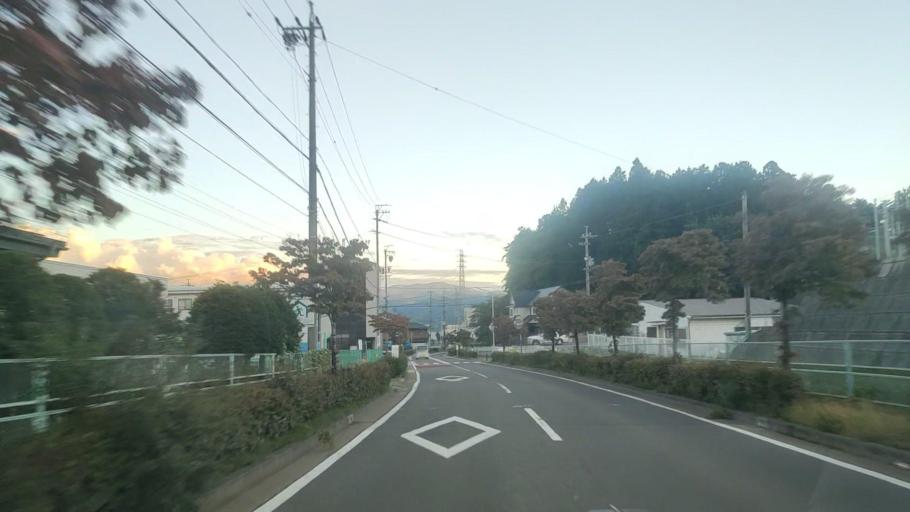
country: JP
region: Nagano
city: Okaya
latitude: 36.0807
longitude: 138.0425
